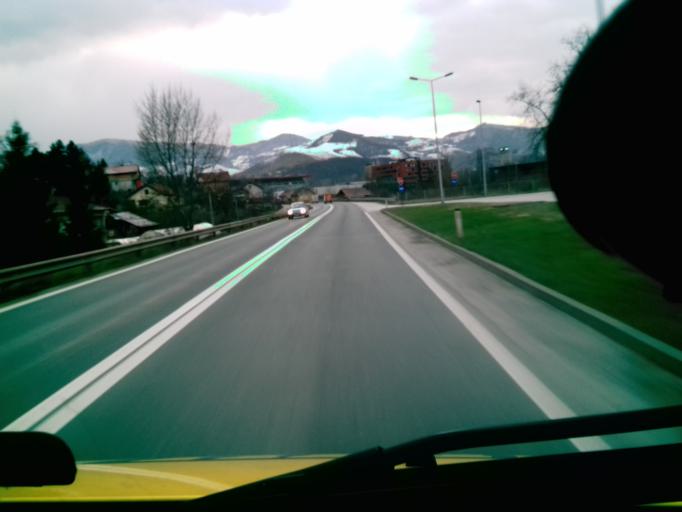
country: BA
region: Federation of Bosnia and Herzegovina
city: Zenica
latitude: 44.2071
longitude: 17.9165
